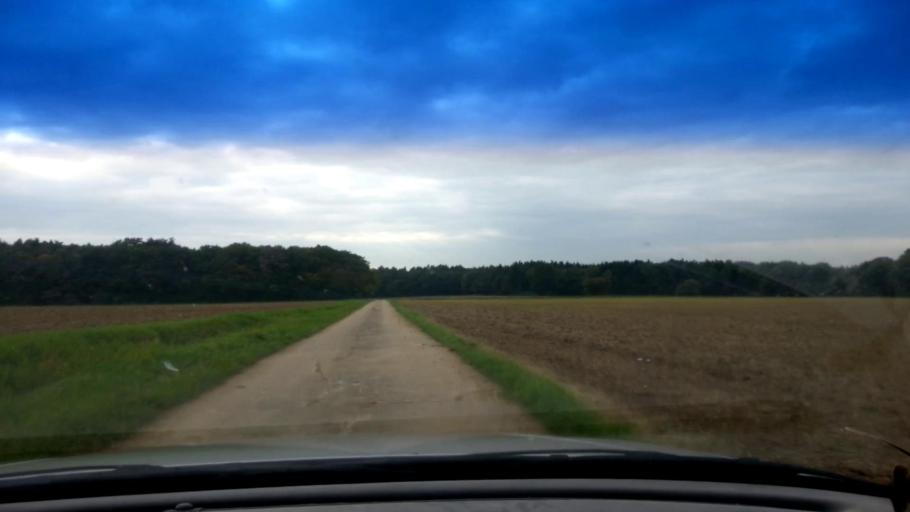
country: DE
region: Bavaria
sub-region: Upper Franconia
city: Memmelsdorf
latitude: 49.9706
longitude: 10.9569
